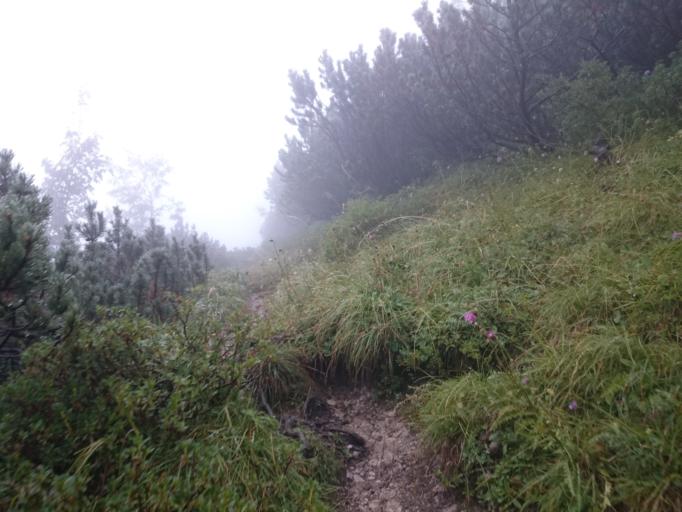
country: AT
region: Tyrol
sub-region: Politischer Bezirk Innsbruck Land
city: Absam
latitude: 47.4110
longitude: 11.5028
